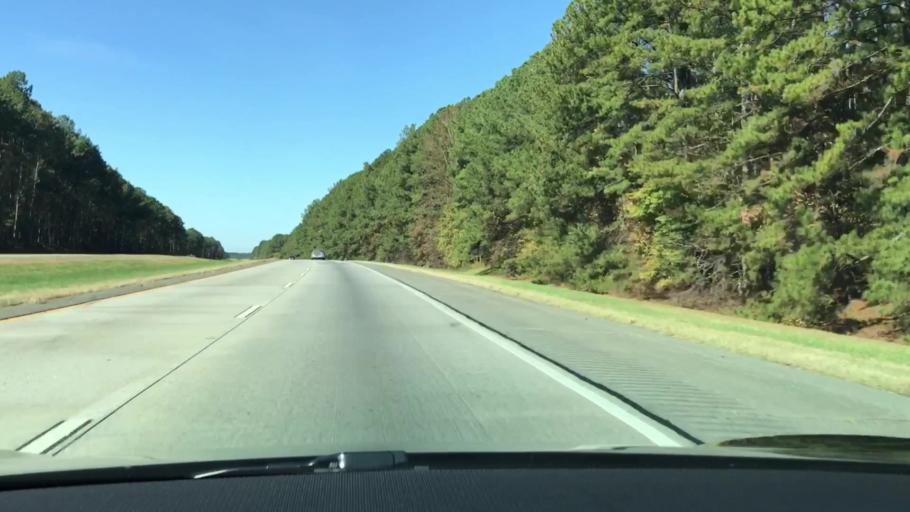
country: US
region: Georgia
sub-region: Taliaferro County
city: Crawfordville
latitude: 33.5240
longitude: -82.8756
